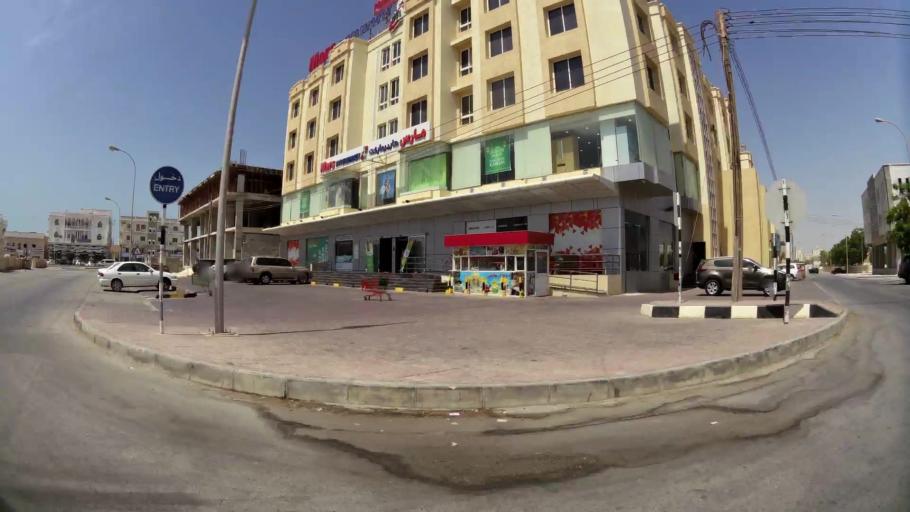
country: OM
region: Zufar
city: Salalah
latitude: 17.0194
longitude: 54.1053
